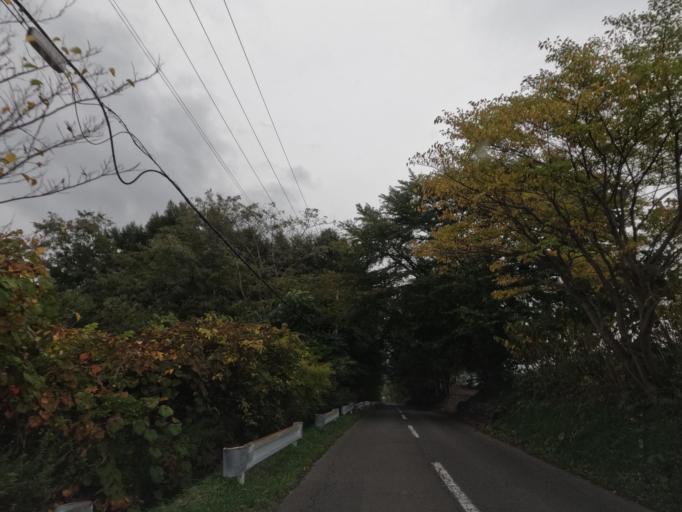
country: JP
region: Hokkaido
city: Date
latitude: 42.4747
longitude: 140.8895
